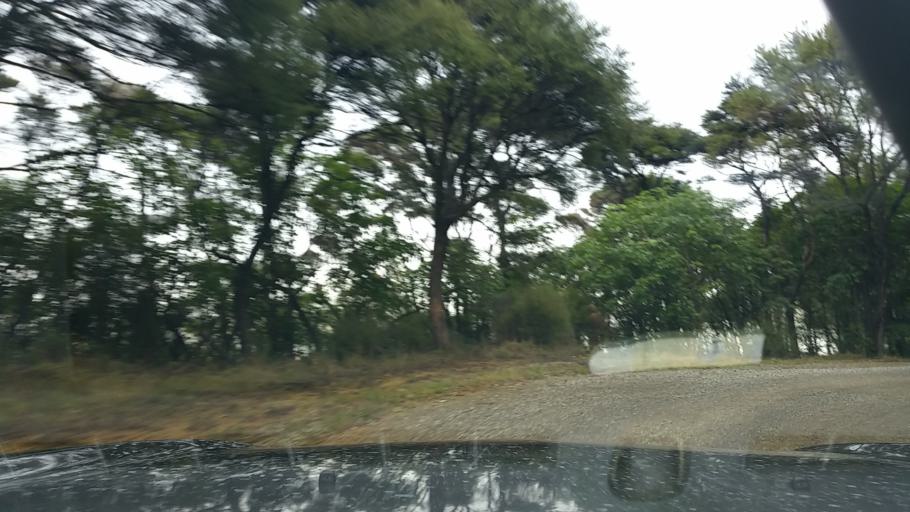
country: NZ
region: Marlborough
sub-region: Marlborough District
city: Picton
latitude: -41.1669
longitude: 174.0123
